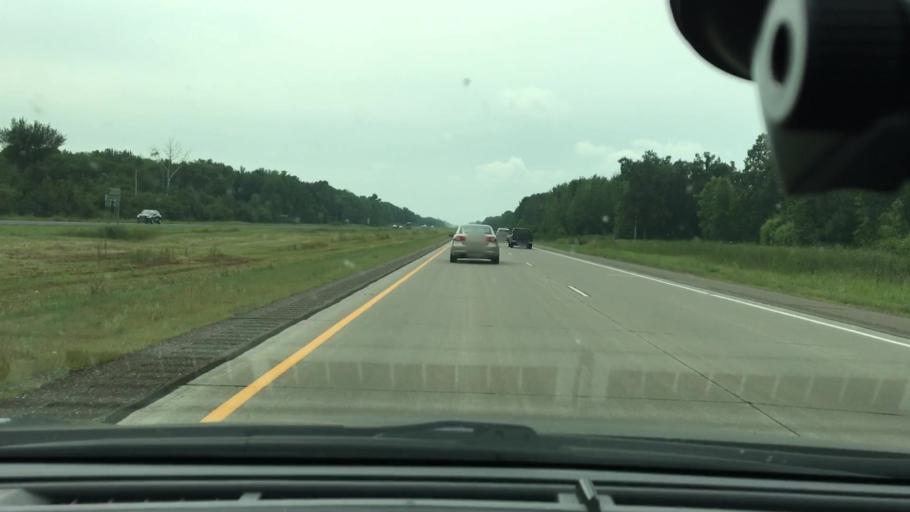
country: US
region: Minnesota
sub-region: Mille Lacs County
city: Vineland
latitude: 46.0249
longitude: -93.6630
